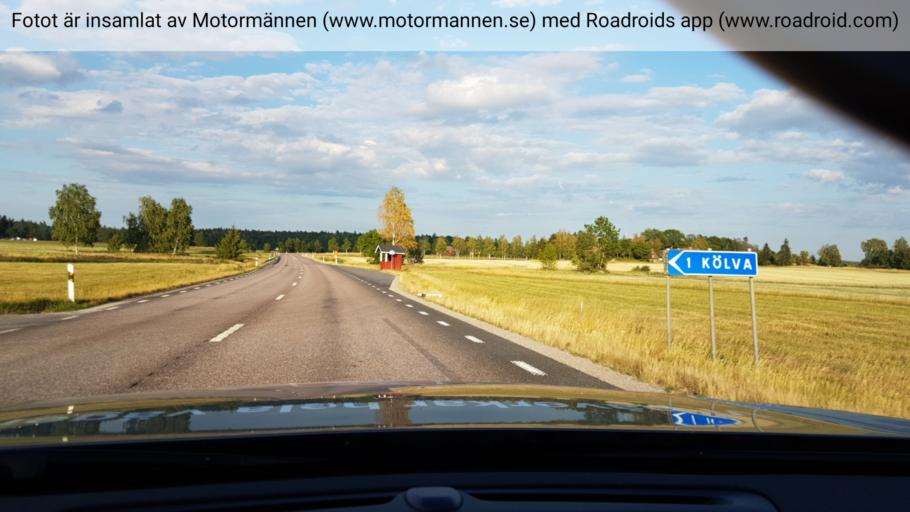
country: SE
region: Uppsala
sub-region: Enkopings Kommun
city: Orsundsbro
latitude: 59.8788
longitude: 17.2695
